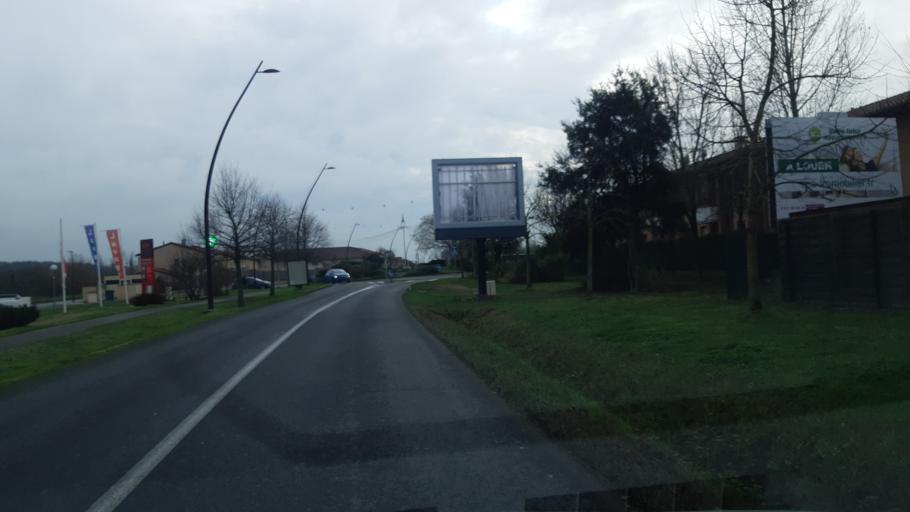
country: FR
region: Midi-Pyrenees
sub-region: Departement de la Haute-Garonne
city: Pibrac
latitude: 43.6087
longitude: 1.2841
